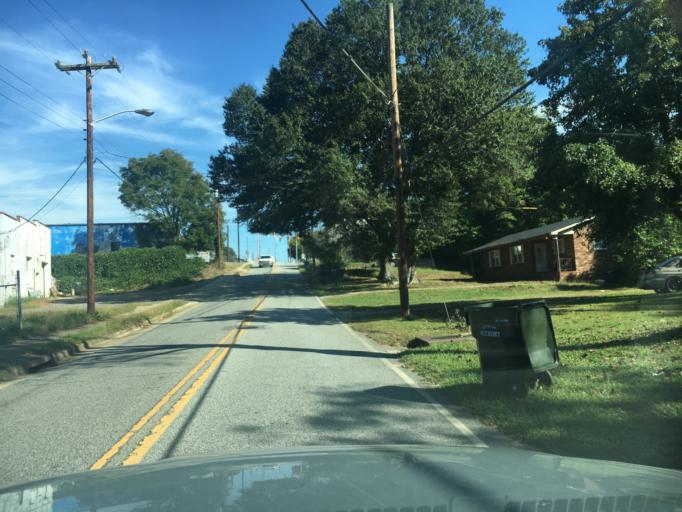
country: US
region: North Carolina
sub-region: Catawba County
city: Hickory
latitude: 35.7288
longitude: -81.3529
